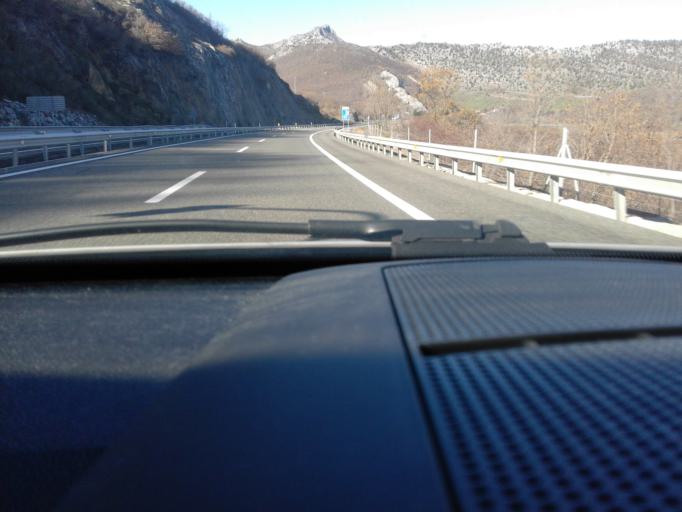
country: ES
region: Castille and Leon
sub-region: Provincia de Leon
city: Soto y Amio
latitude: 42.8634
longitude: -5.8758
